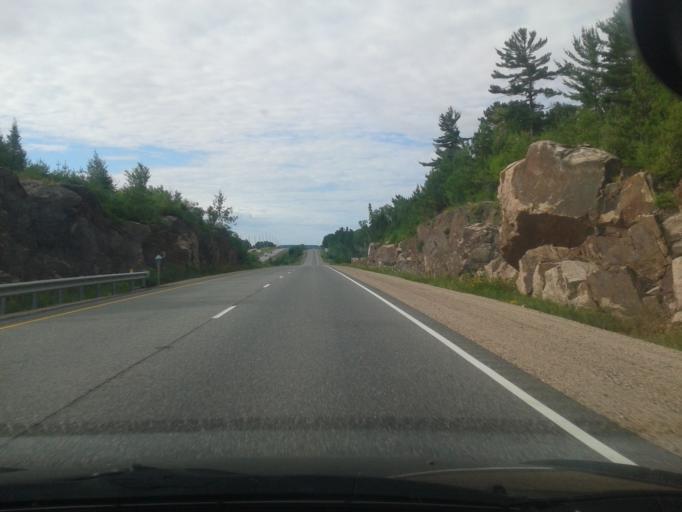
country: CA
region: Ontario
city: Powassan
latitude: 46.1144
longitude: -79.3656
